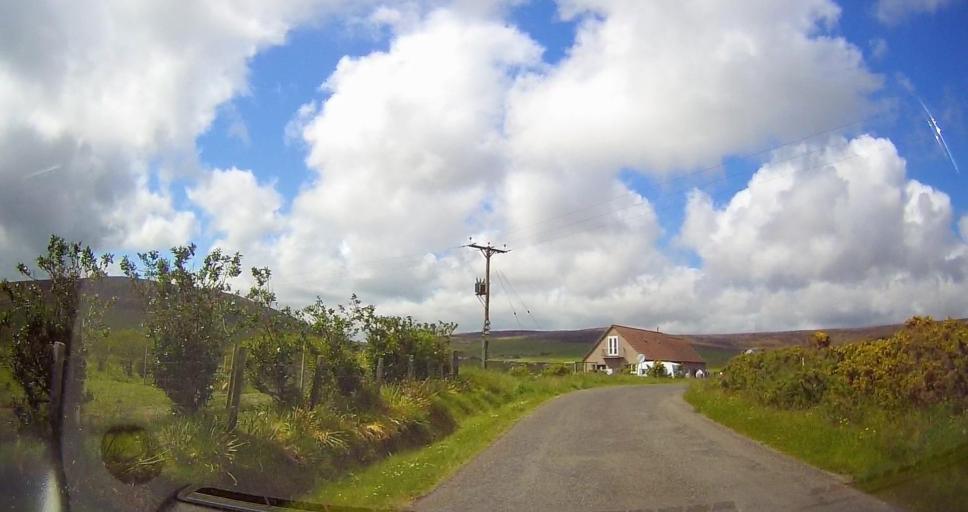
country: GB
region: Scotland
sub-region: Orkney Islands
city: Orkney
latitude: 59.0478
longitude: -3.0829
